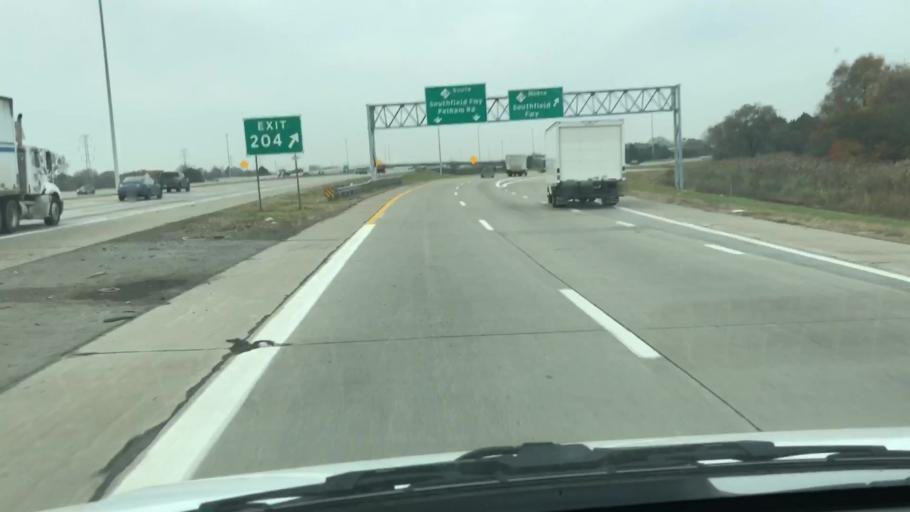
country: US
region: Michigan
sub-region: Wayne County
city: Allen Park
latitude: 42.2686
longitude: -83.2171
